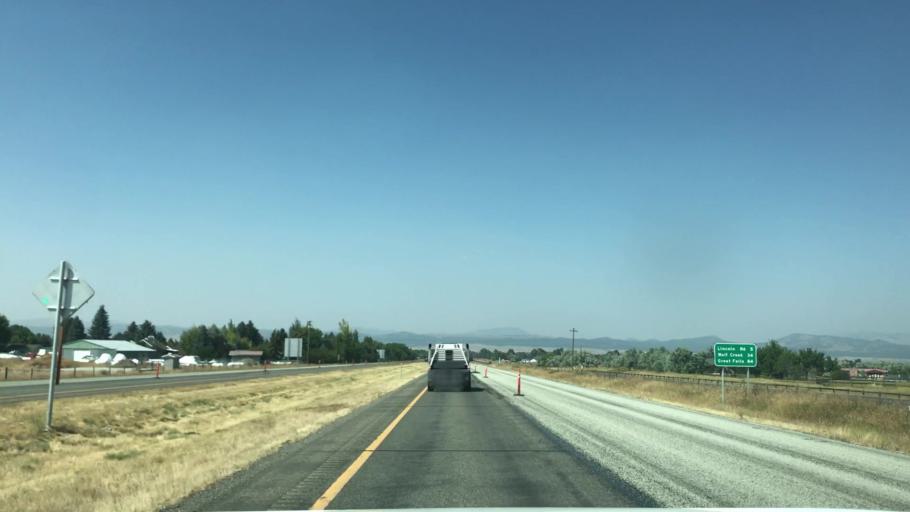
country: US
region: Montana
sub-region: Lewis and Clark County
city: Helena
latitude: 46.6290
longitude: -112.0110
